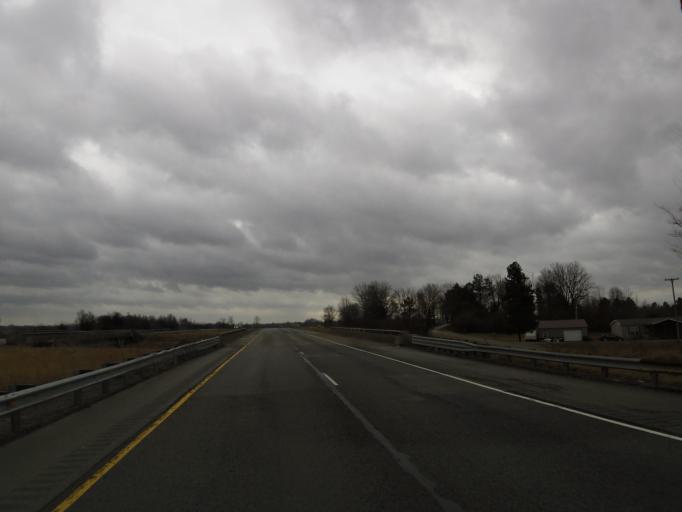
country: US
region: Illinois
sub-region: Massac County
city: Metropolis
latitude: 37.1916
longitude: -88.6860
